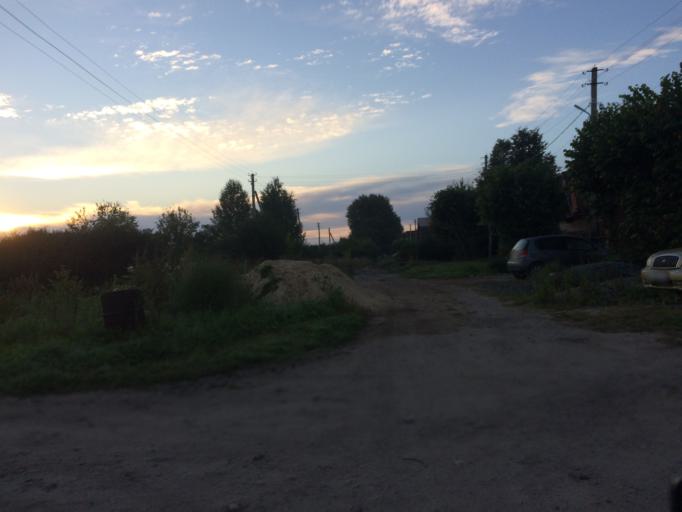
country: RU
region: Mariy-El
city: Yoshkar-Ola
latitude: 56.6549
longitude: 47.9063
